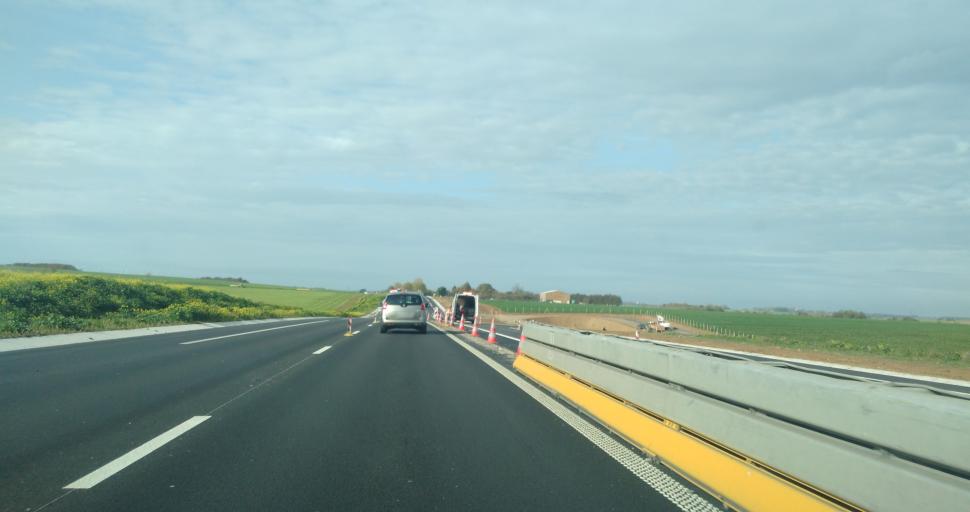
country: FR
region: Nord-Pas-de-Calais
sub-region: Departement du Pas-de-Calais
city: Aubigny-en-Artois
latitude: 50.3404
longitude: 2.6030
